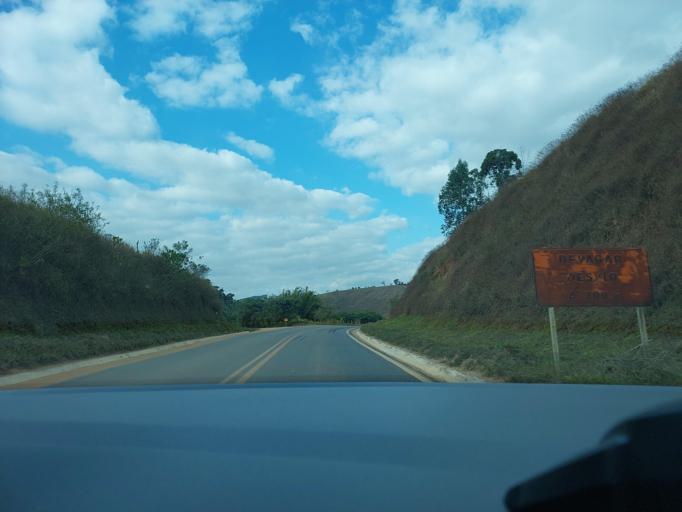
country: BR
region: Minas Gerais
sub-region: Visconde Do Rio Branco
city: Visconde do Rio Branco
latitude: -20.8523
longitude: -42.6725
